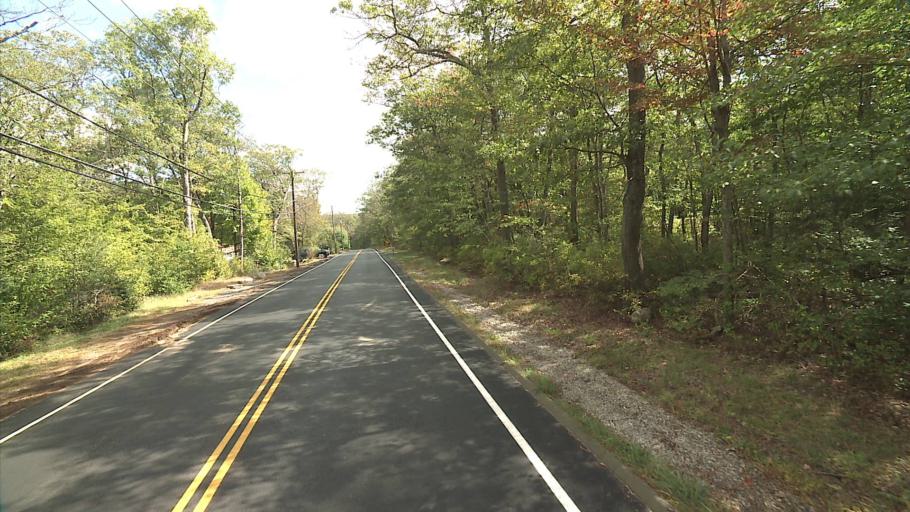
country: US
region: Connecticut
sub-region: Middlesex County
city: Chester Center
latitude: 41.3902
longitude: -72.5587
